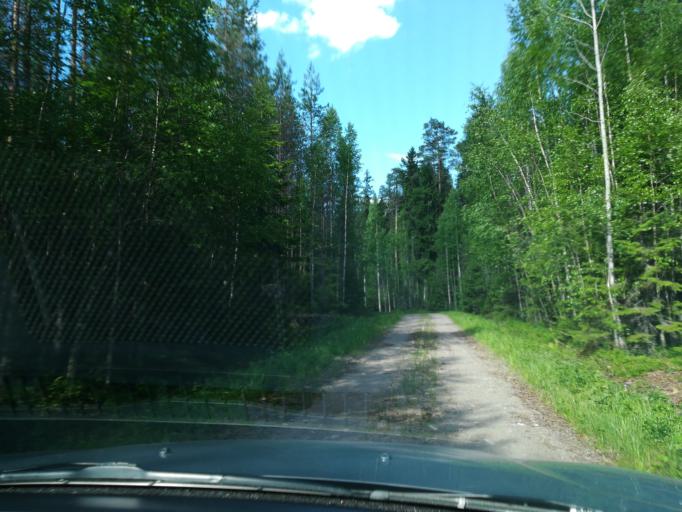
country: FI
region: South Karelia
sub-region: Imatra
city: Ruokolahti
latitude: 61.5486
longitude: 28.8109
